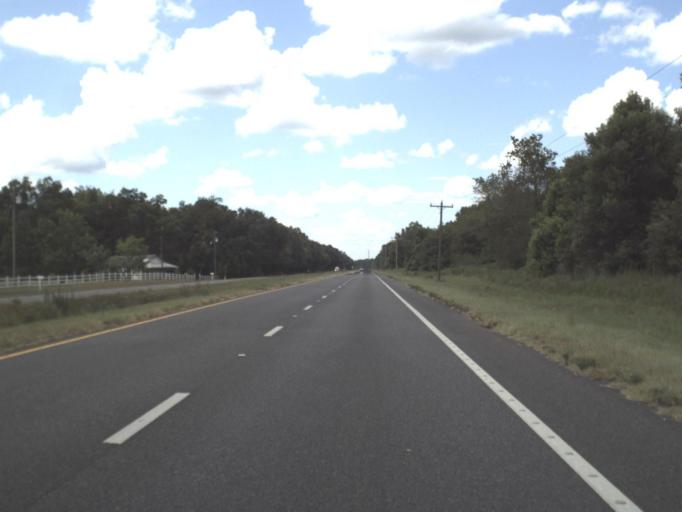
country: US
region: Florida
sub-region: Taylor County
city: Perry
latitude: 30.1731
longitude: -83.6321
